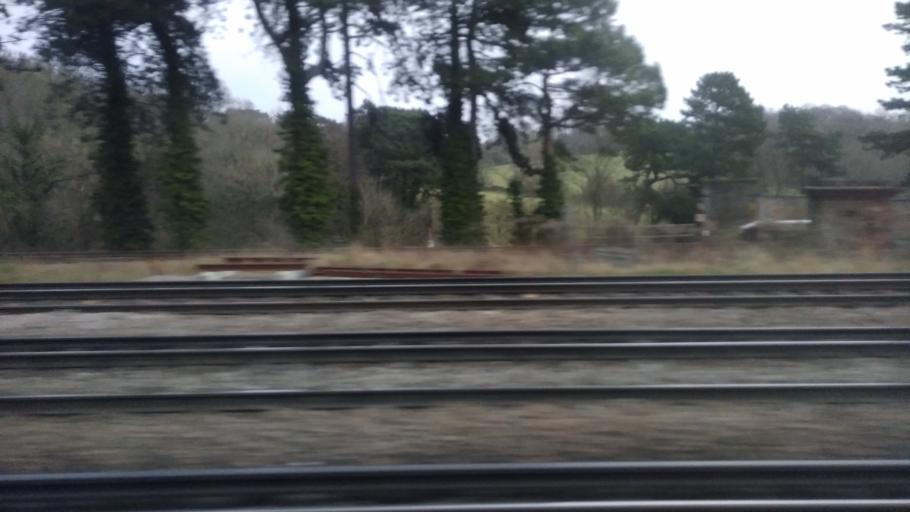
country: GB
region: England
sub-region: Greater London
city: Chislehurst
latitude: 51.4027
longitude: 0.0606
